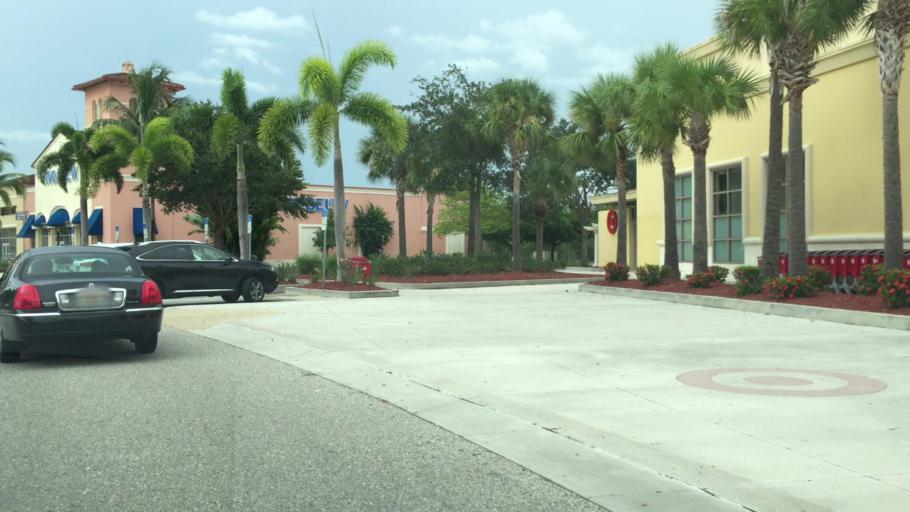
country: US
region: Florida
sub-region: Lee County
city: Estero
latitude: 26.4069
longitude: -81.8062
